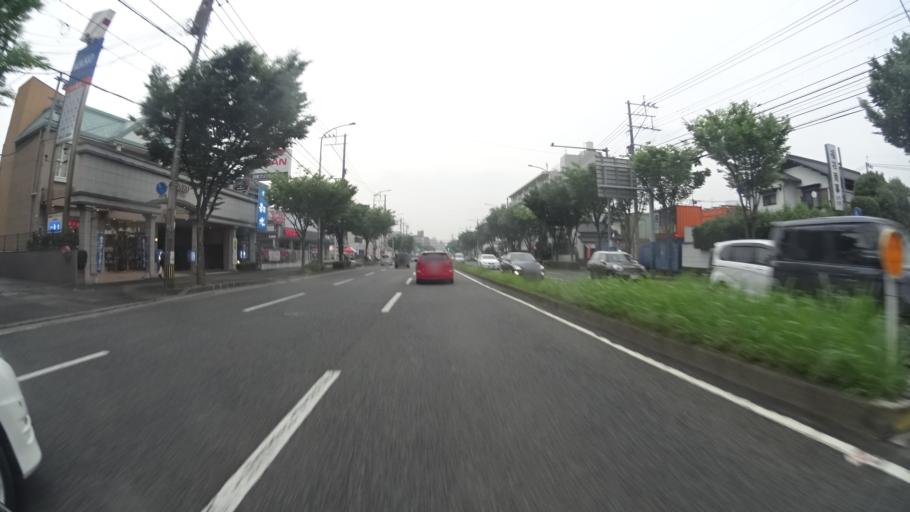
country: JP
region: Fukuoka
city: Onojo
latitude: 33.5494
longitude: 130.4409
